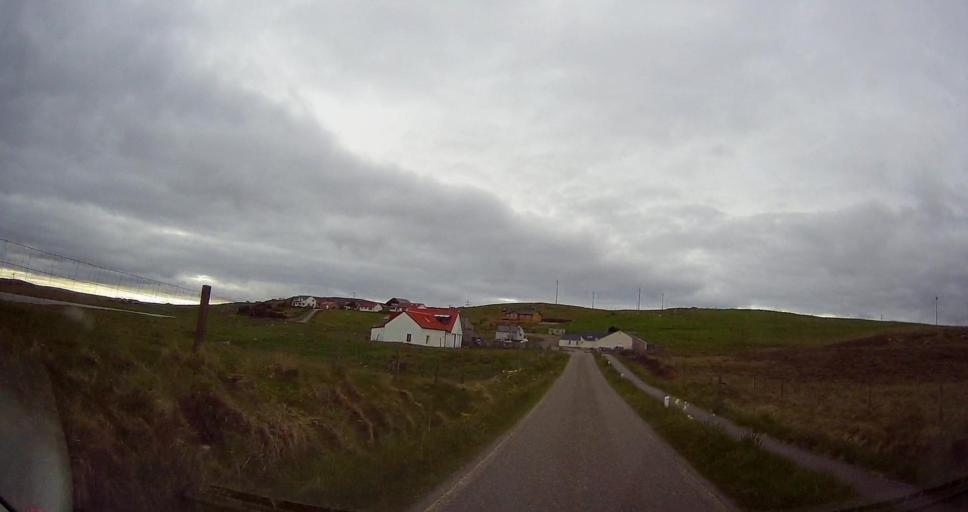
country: GB
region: Scotland
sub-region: Shetland Islands
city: Shetland
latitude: 60.5006
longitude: -1.0608
